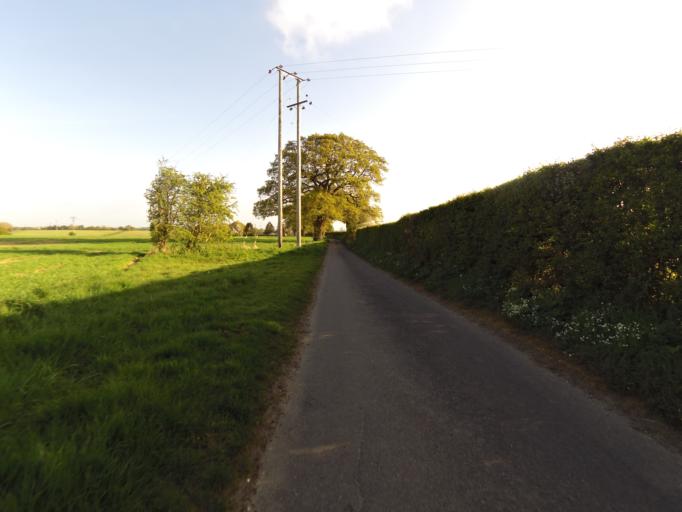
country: GB
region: England
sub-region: Suffolk
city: Capel Saint Mary
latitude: 52.0371
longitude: 1.0721
